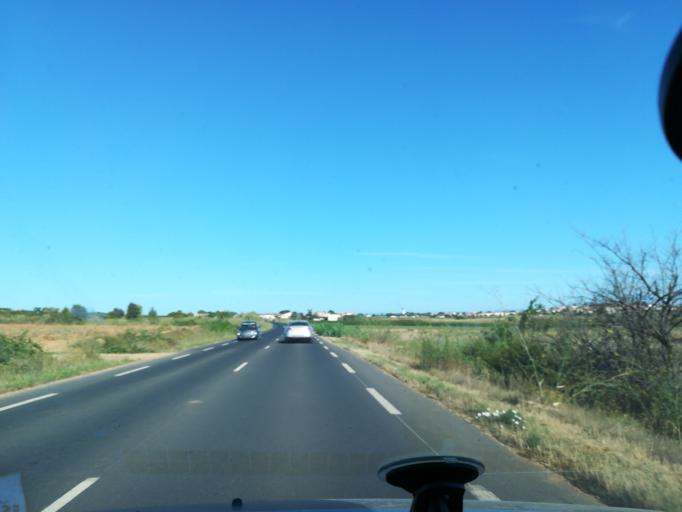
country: FR
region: Languedoc-Roussillon
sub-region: Departement de l'Herault
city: Portiragnes
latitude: 43.2958
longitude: 3.3528
